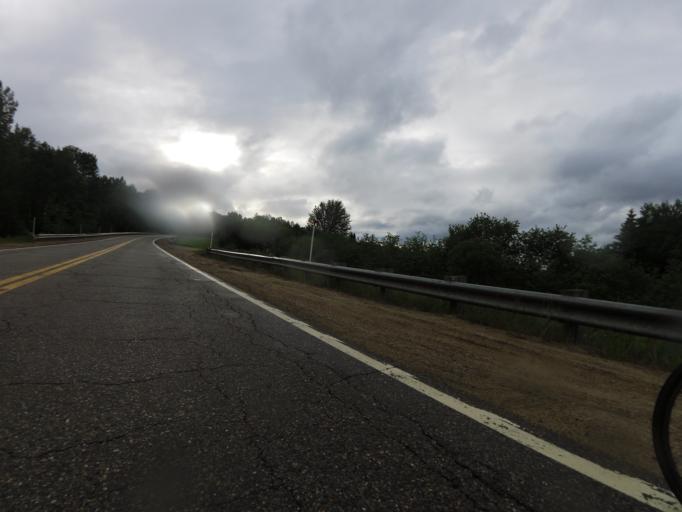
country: CA
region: Quebec
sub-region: Outaouais
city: Shawville
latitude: 45.9054
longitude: -76.2756
